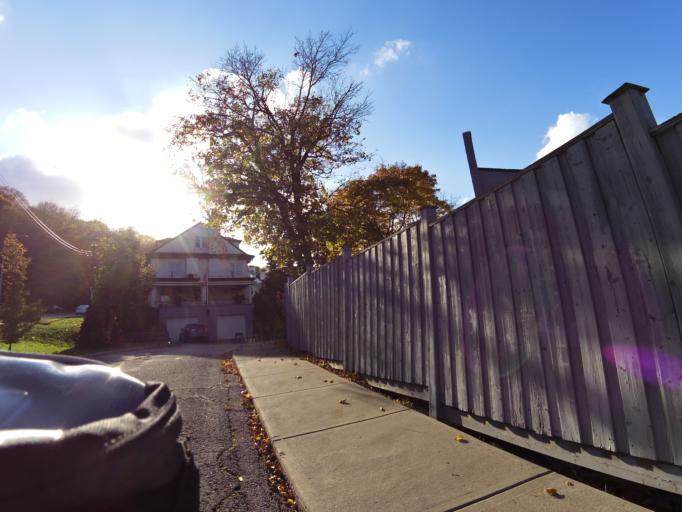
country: CA
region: Ontario
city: Hamilton
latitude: 43.2465
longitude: -79.8749
